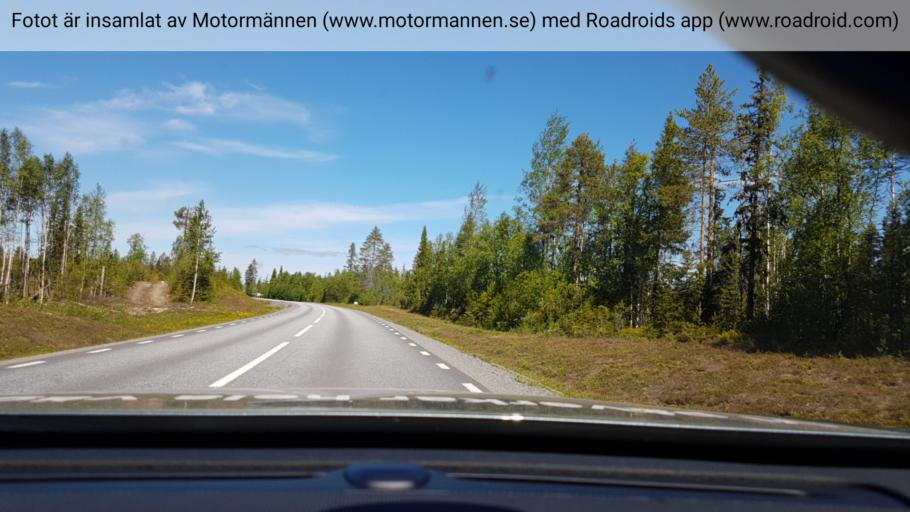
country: SE
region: Vaesterbotten
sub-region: Vilhelmina Kommun
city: Vilhelmina
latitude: 64.5042
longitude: 16.7747
